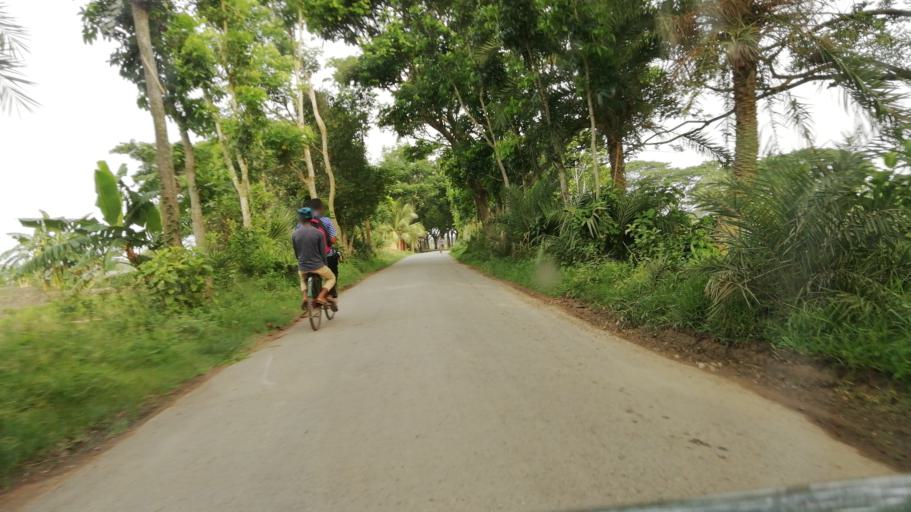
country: BD
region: Khulna
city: Bhatpara Abhaynagar
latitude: 23.0401
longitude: 89.3208
